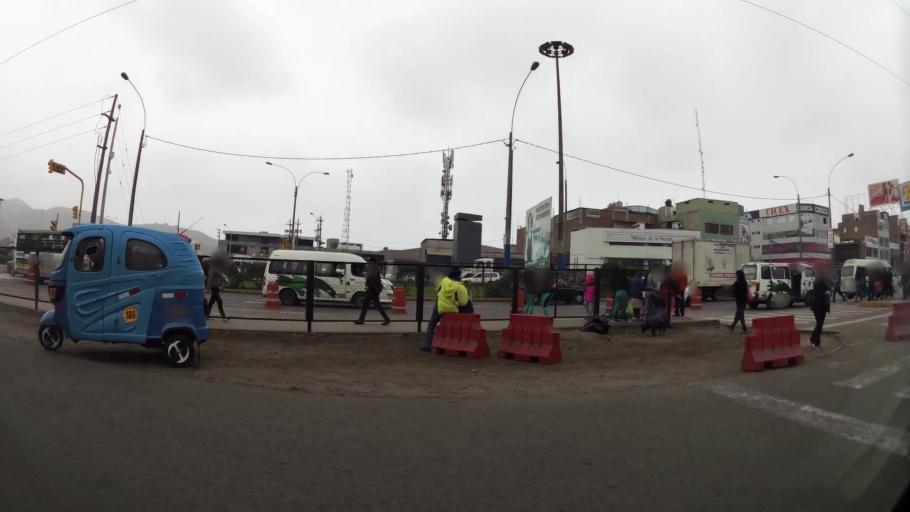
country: PE
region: Lima
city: Ventanilla
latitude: -11.8762
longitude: -77.1264
